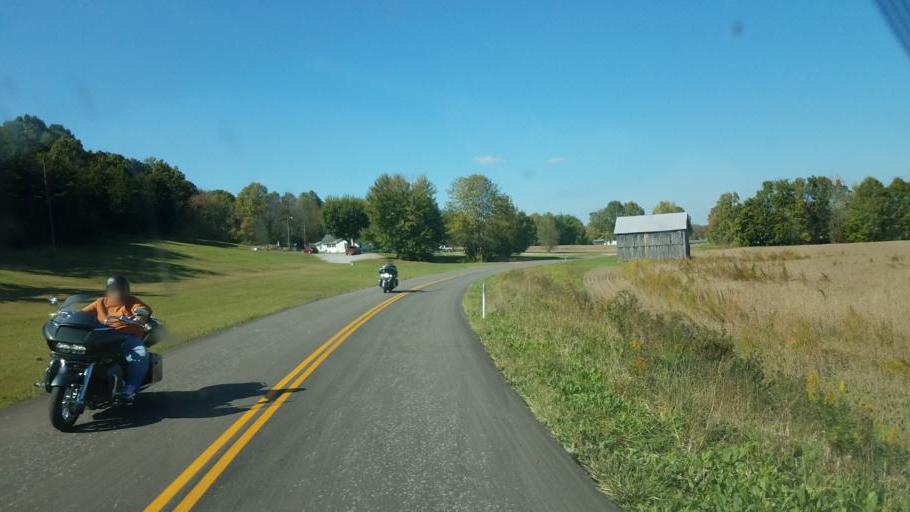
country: US
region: Kentucky
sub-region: Fleming County
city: Flemingsburg
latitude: 38.4632
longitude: -83.5862
